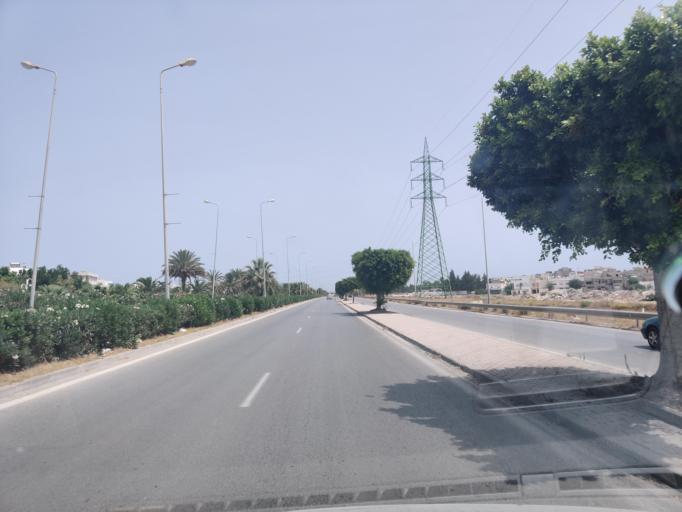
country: TN
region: Tunis
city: Carthage
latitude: 36.8518
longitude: 10.3067
